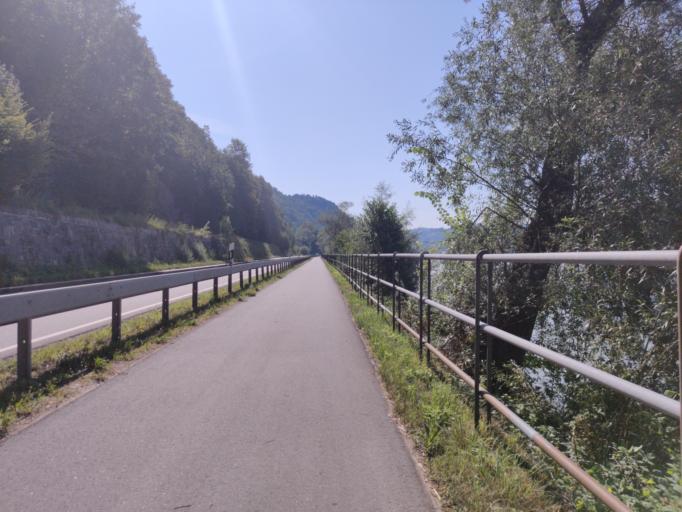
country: DE
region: Bavaria
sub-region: Lower Bavaria
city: Thyrnau
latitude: 48.5823
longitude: 13.5368
